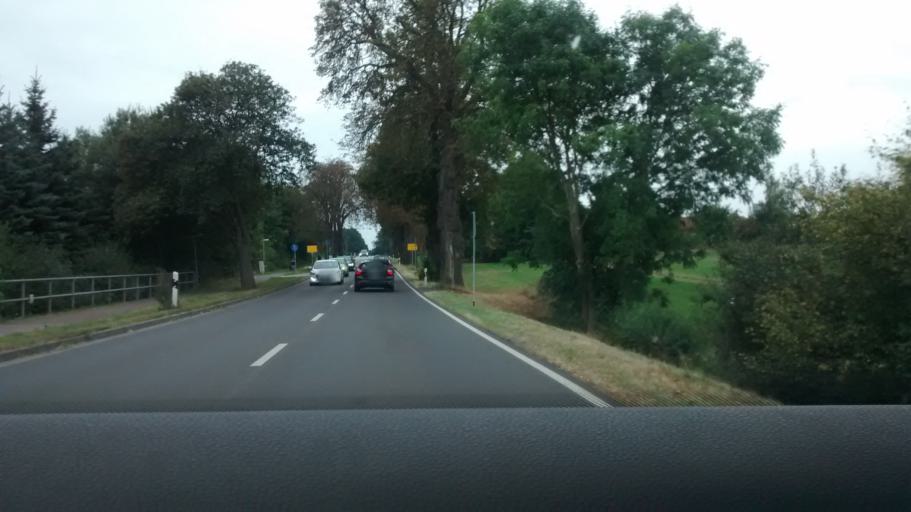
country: DE
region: Mecklenburg-Vorpommern
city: Mecklenburg
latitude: 53.8492
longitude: 11.4577
